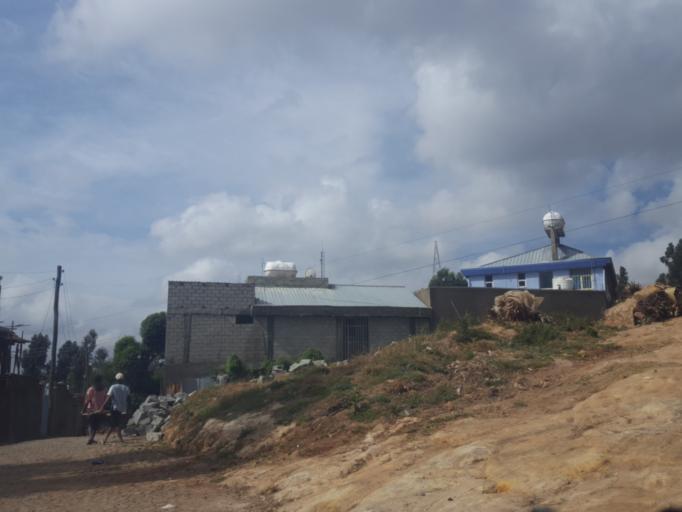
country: ET
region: Adis Abeba
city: Addis Ababa
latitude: 9.0670
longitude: 38.7459
